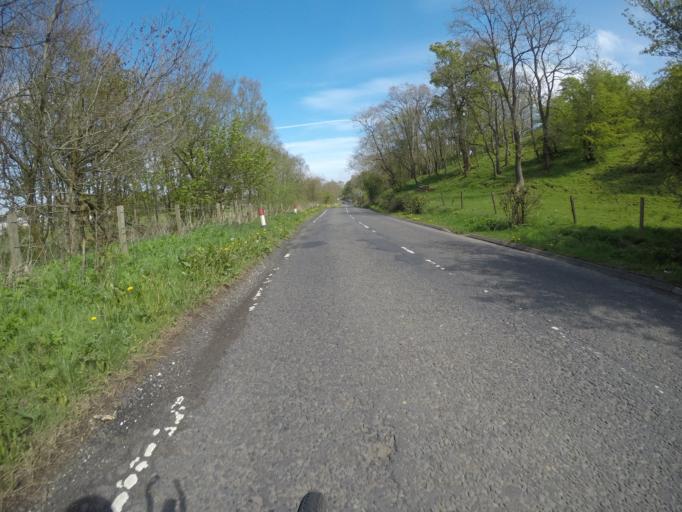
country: GB
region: Scotland
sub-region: East Ayrshire
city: Stewarton
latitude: 55.6730
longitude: -4.5262
